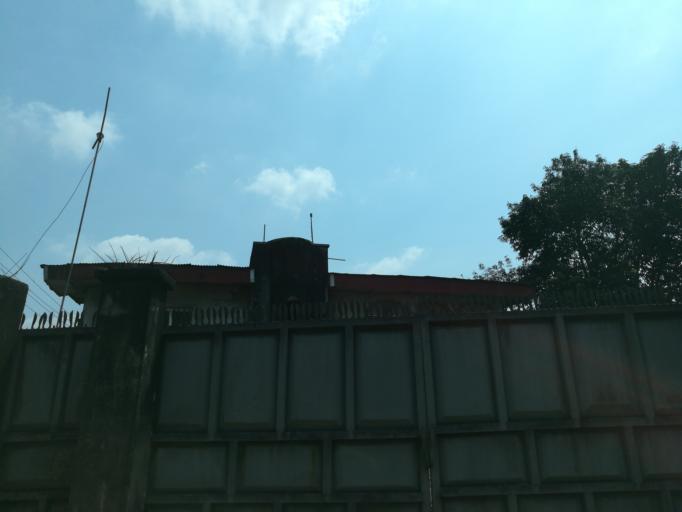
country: NG
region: Rivers
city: Port Harcourt
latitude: 4.8087
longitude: 6.9831
